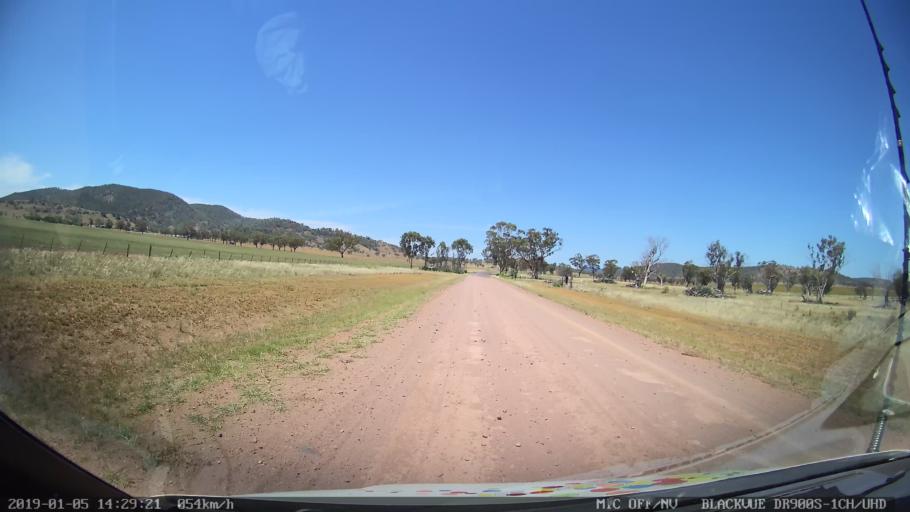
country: AU
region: New South Wales
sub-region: Tamworth Municipality
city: Phillip
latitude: -31.2293
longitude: 150.5810
